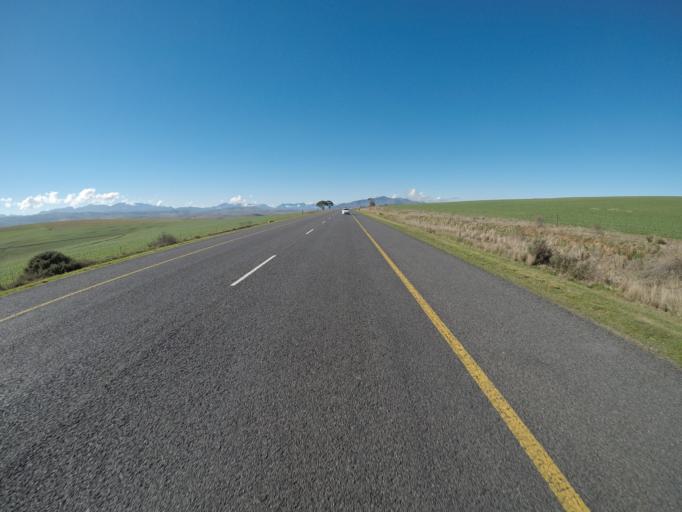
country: ZA
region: Western Cape
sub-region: Overberg District Municipality
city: Caledon
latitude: -34.2235
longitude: 19.3006
